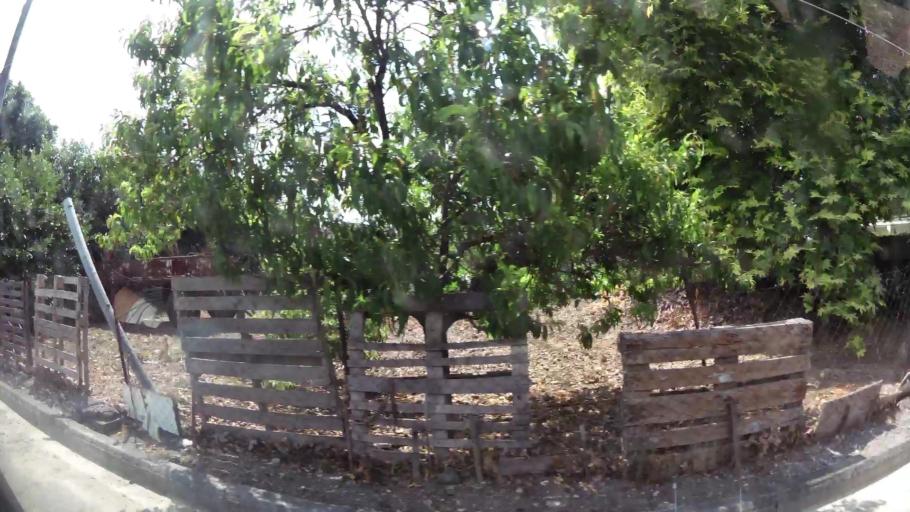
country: GR
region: Central Macedonia
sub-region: Nomos Pierias
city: Korinos
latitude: 40.3173
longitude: 22.5801
